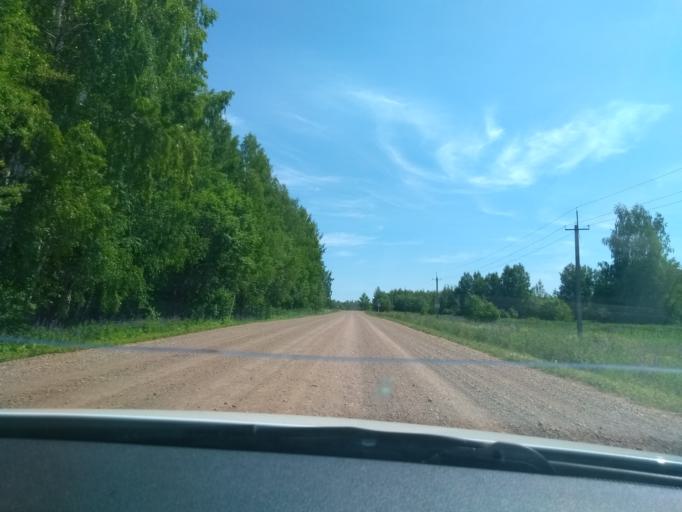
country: RU
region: Perm
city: Sylva
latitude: 57.8173
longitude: 56.7248
